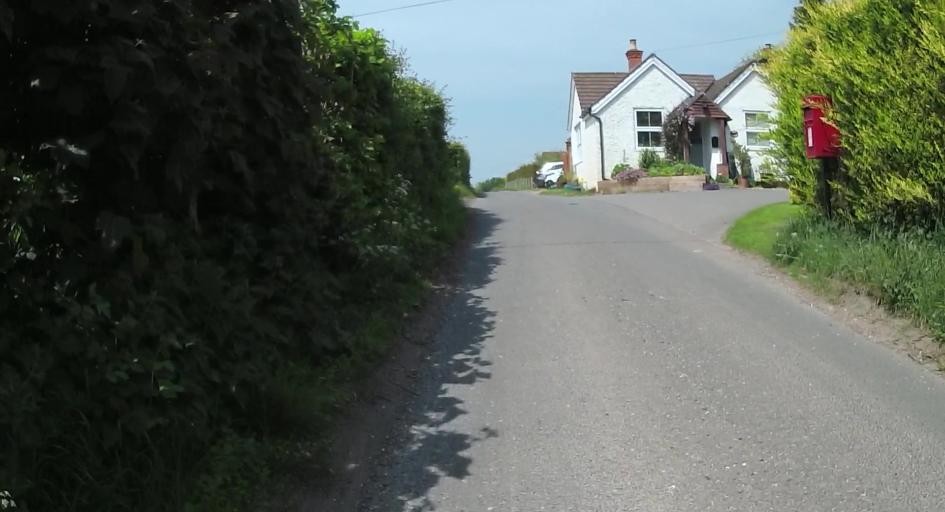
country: GB
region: England
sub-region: Hampshire
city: Overton
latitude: 51.2620
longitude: -1.2321
